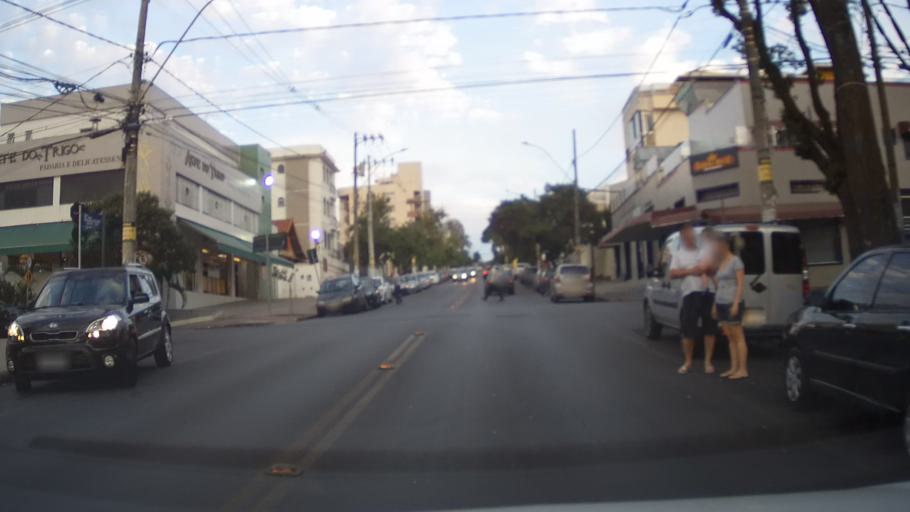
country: BR
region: Minas Gerais
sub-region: Belo Horizonte
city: Belo Horizonte
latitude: -19.8885
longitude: -43.9240
